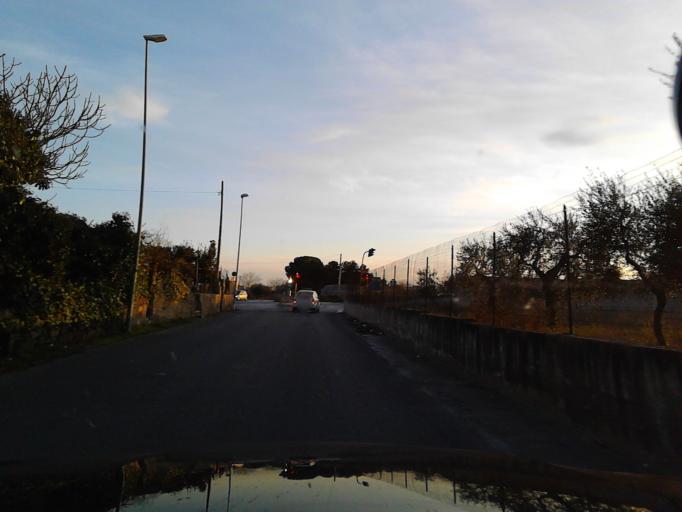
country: IT
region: Apulia
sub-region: Provincia di Bari
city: Triggiano
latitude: 41.0573
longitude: 16.9215
